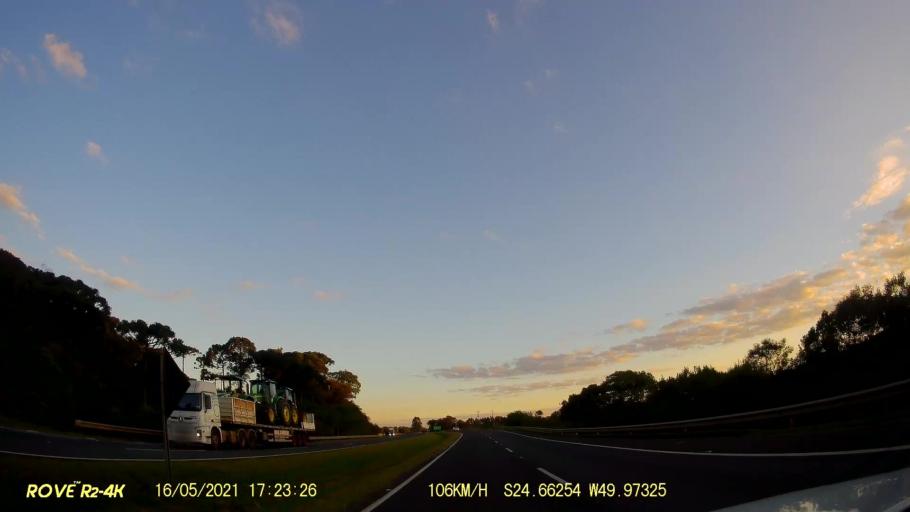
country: BR
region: Parana
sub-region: Castro
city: Castro
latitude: -24.6627
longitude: -49.9733
